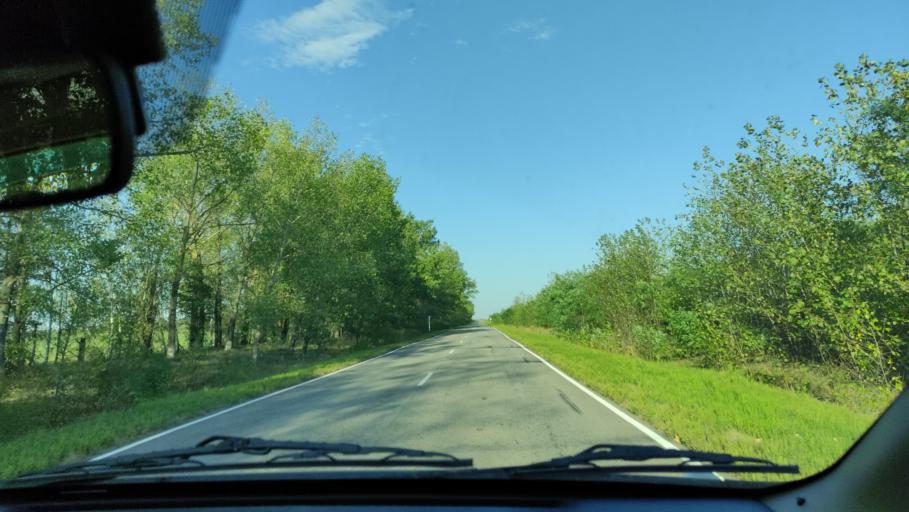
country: RU
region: Voronezj
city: Verkhniy Mamon
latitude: 50.1207
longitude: 40.3024
